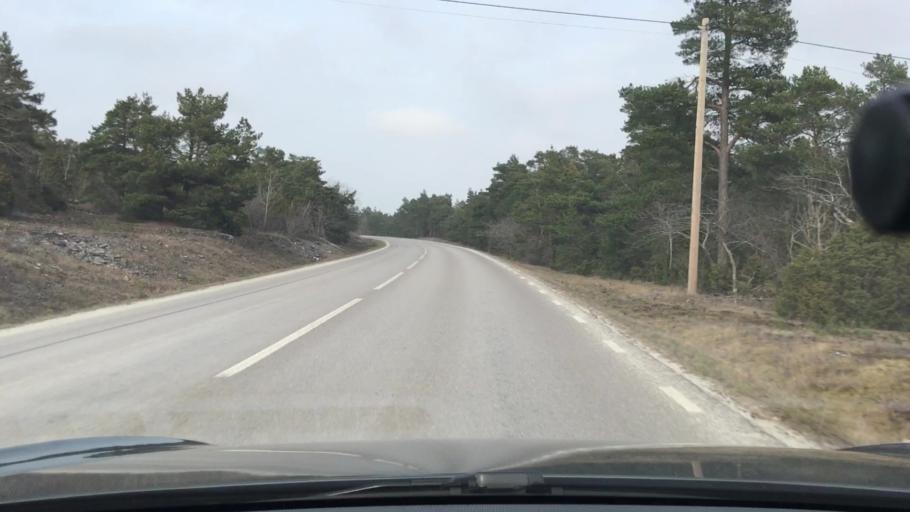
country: SE
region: Gotland
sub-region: Gotland
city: Slite
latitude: 57.4377
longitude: 18.6950
